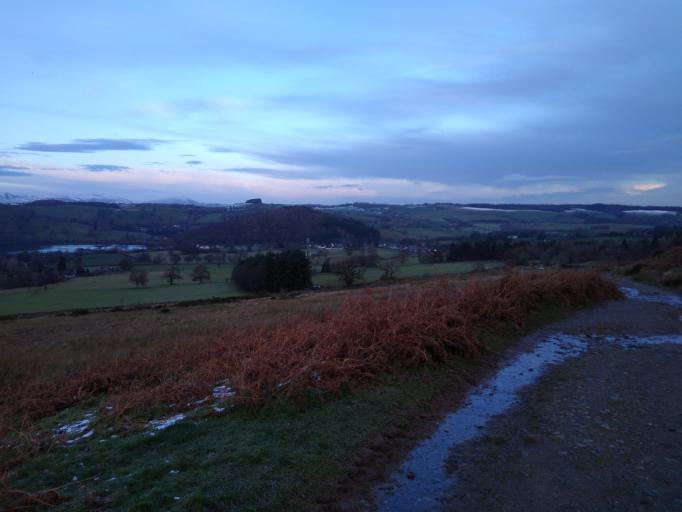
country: GB
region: England
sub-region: Cumbria
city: Penrith
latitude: 54.6023
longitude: -2.8075
